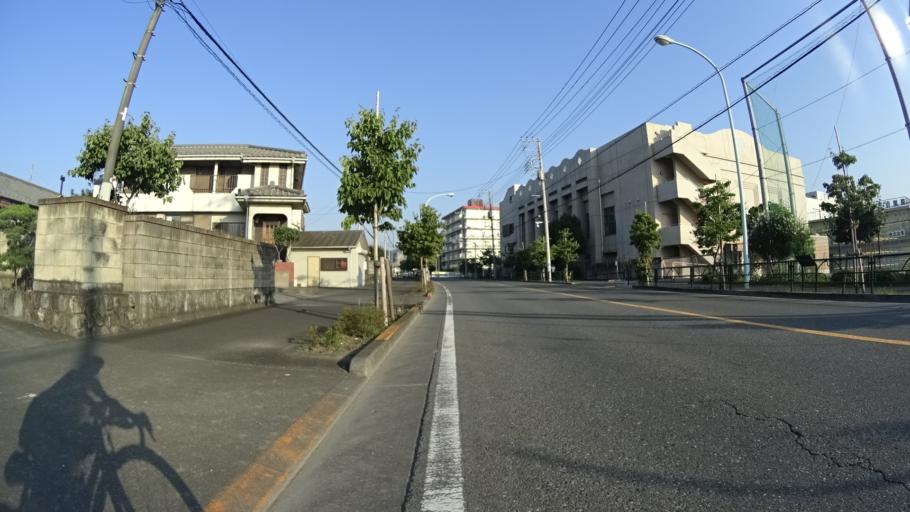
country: JP
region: Tokyo
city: Ome
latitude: 35.7798
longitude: 139.2708
